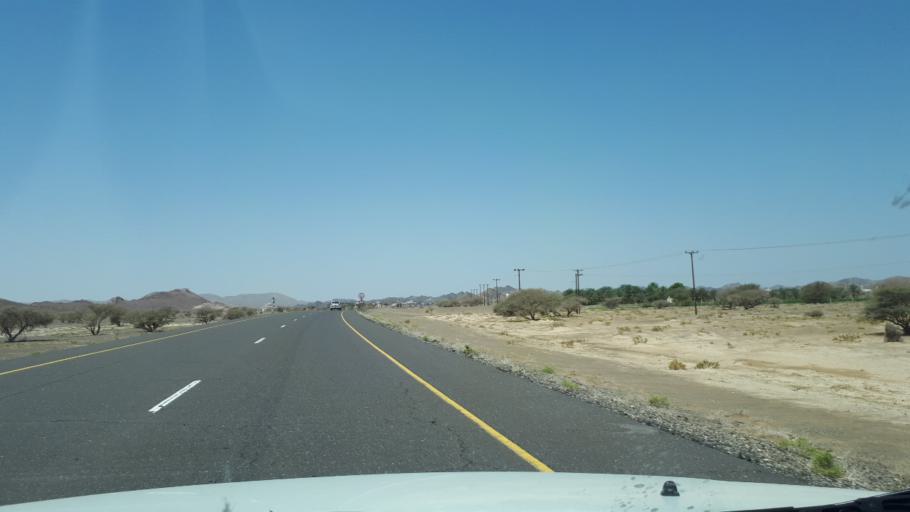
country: OM
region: Ash Sharqiyah
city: Ibra'
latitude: 22.6180
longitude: 58.4015
